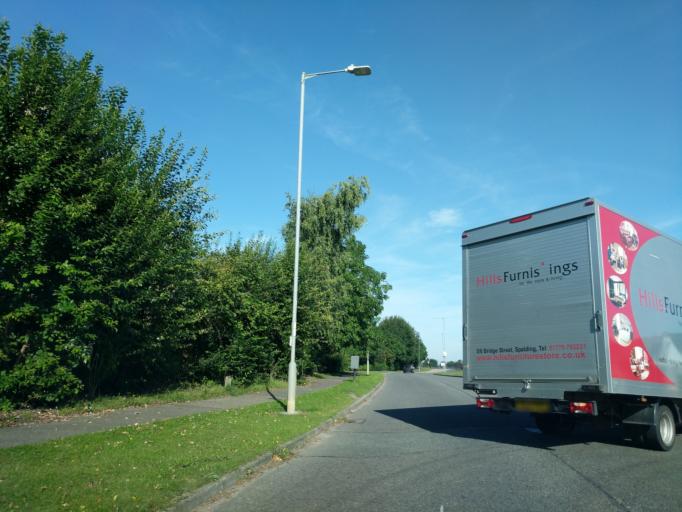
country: GB
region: England
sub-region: Lincolnshire
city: Spalding
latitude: 52.7806
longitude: -0.1749
